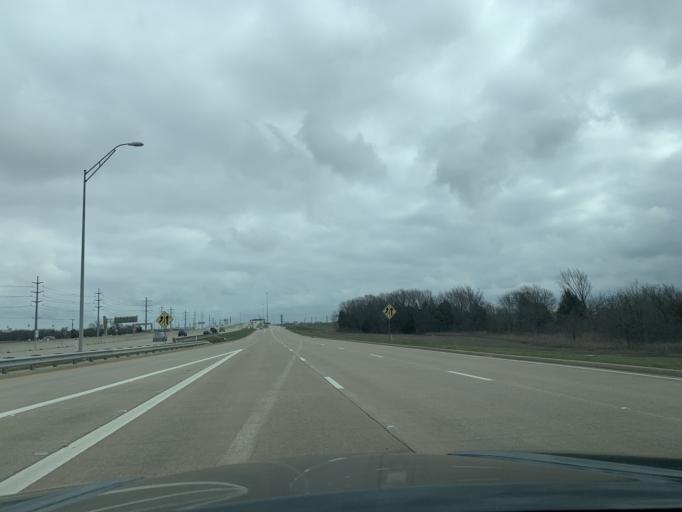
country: US
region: Texas
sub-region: Collin County
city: Fairview
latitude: 33.1469
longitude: -96.6723
